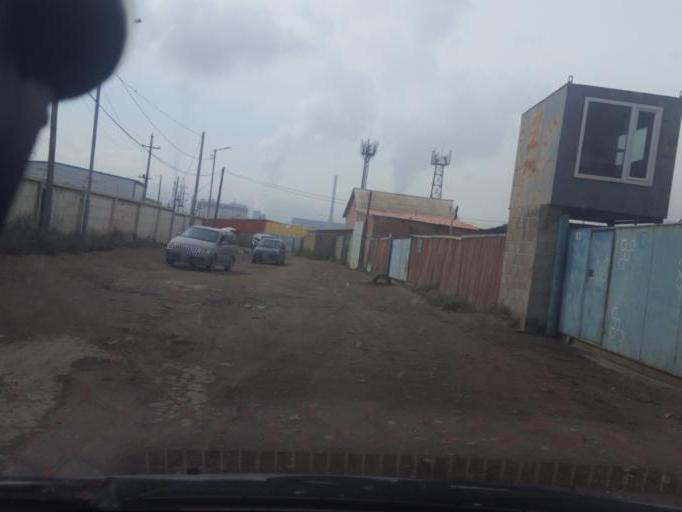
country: MN
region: Ulaanbaatar
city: Ulaanbaatar
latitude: 47.9196
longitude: 106.7989
